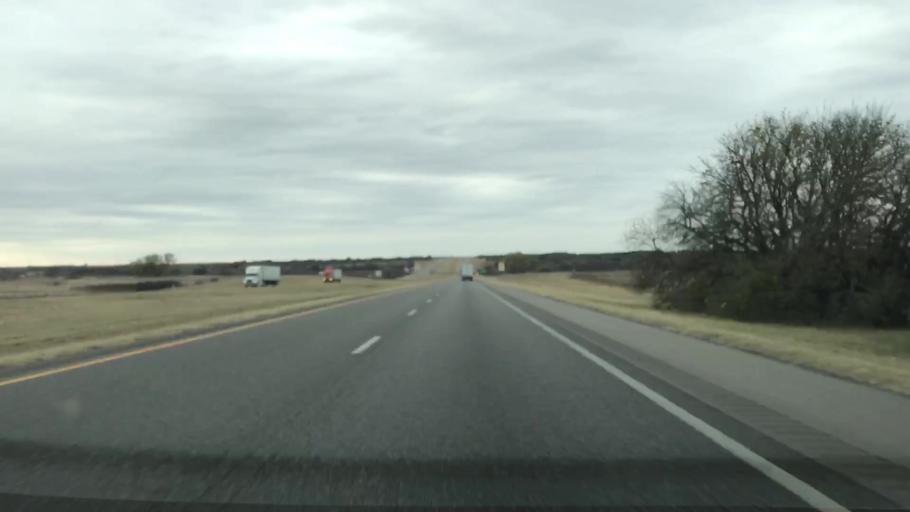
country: US
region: Oklahoma
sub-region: Beckham County
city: Erick
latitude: 35.2266
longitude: -99.8847
